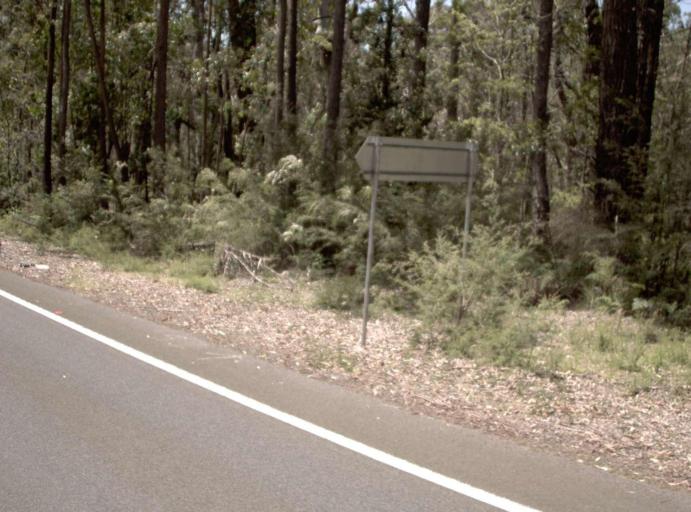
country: AU
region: Victoria
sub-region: East Gippsland
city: Lakes Entrance
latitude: -37.7451
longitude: 148.0738
